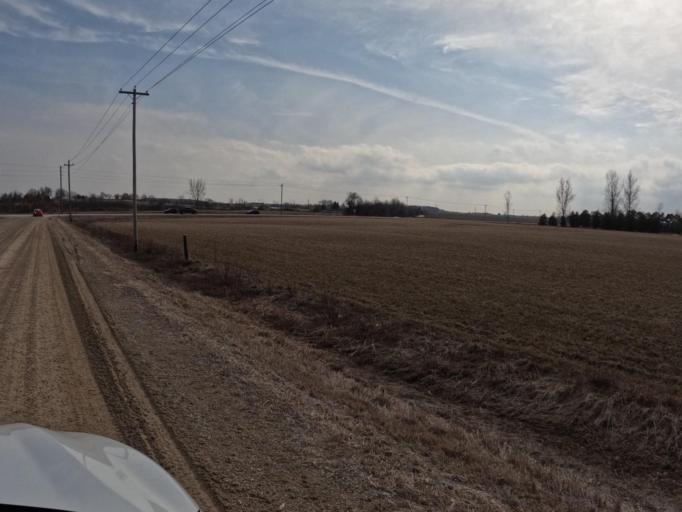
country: CA
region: Ontario
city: Orangeville
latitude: 43.8786
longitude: -80.2964
